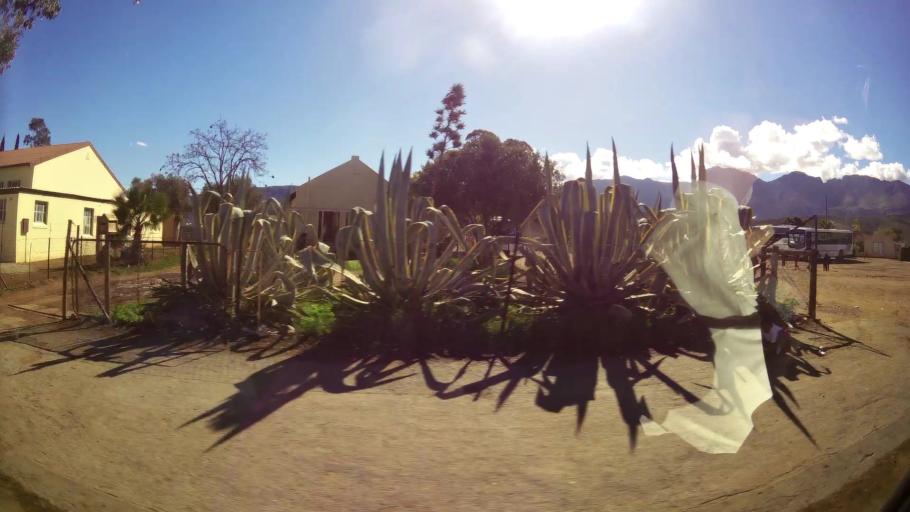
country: ZA
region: Western Cape
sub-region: Cape Winelands District Municipality
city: Ashton
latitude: -33.7943
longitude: 19.8862
